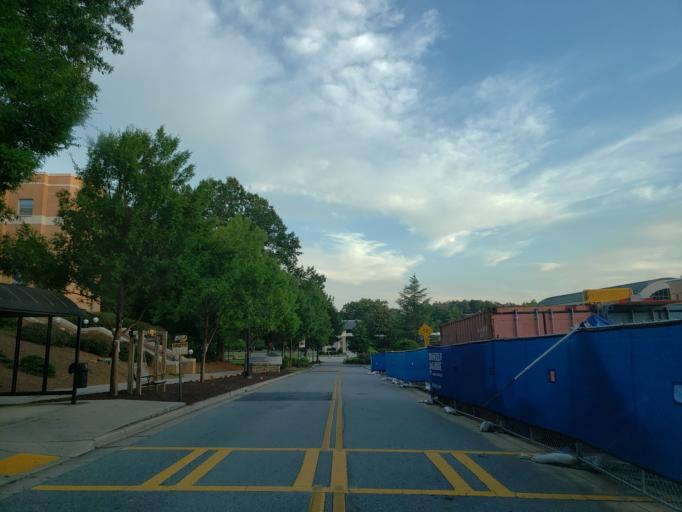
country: US
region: Georgia
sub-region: Cobb County
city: Kennesaw
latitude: 34.0398
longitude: -84.5825
